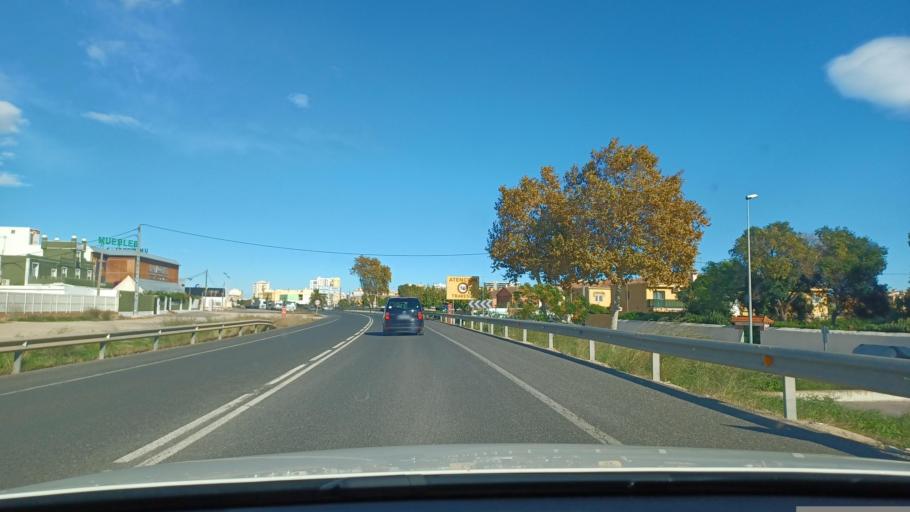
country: ES
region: Valencia
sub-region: Provincia de Castello
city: Vinaros
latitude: 40.4601
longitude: 0.4614
